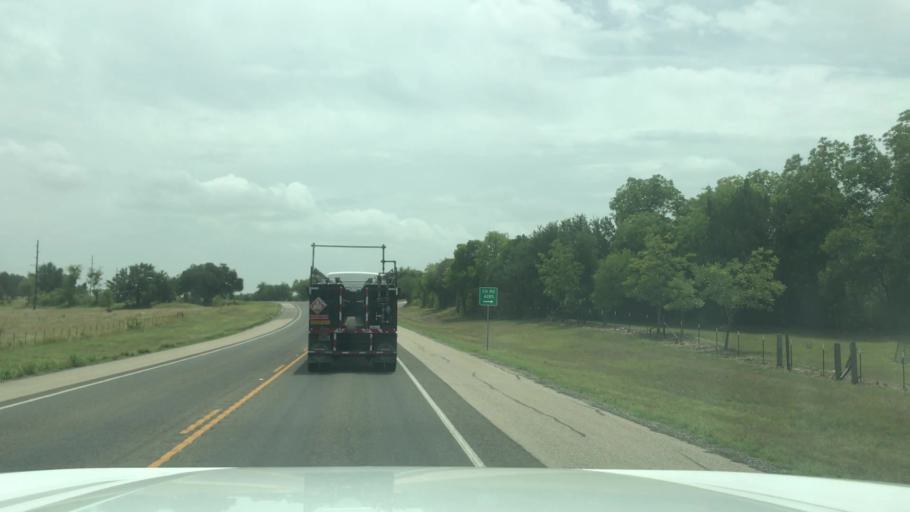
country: US
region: Texas
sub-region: Bosque County
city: Clifton
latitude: 31.7084
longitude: -97.5455
